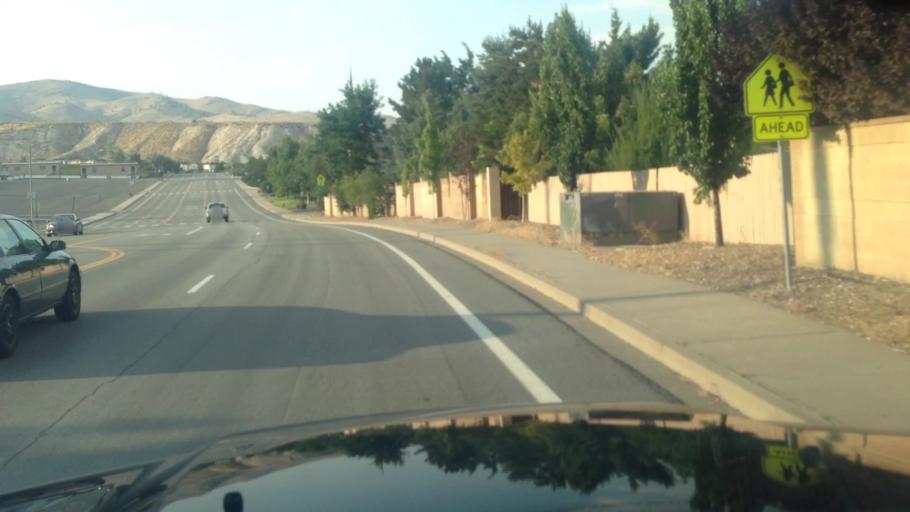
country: US
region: Nevada
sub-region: Washoe County
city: Mogul
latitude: 39.5325
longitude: -119.8819
